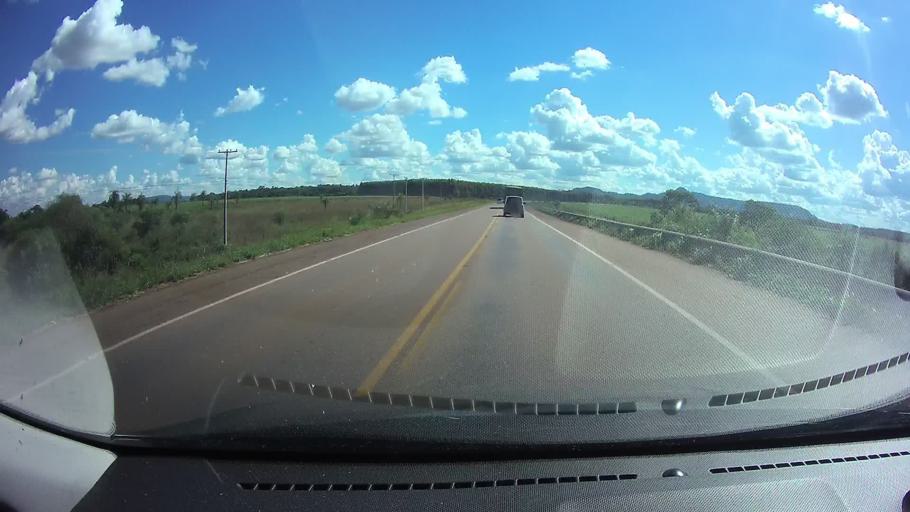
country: PY
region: Guaira
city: Coronel Martinez
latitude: -25.7602
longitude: -56.7189
